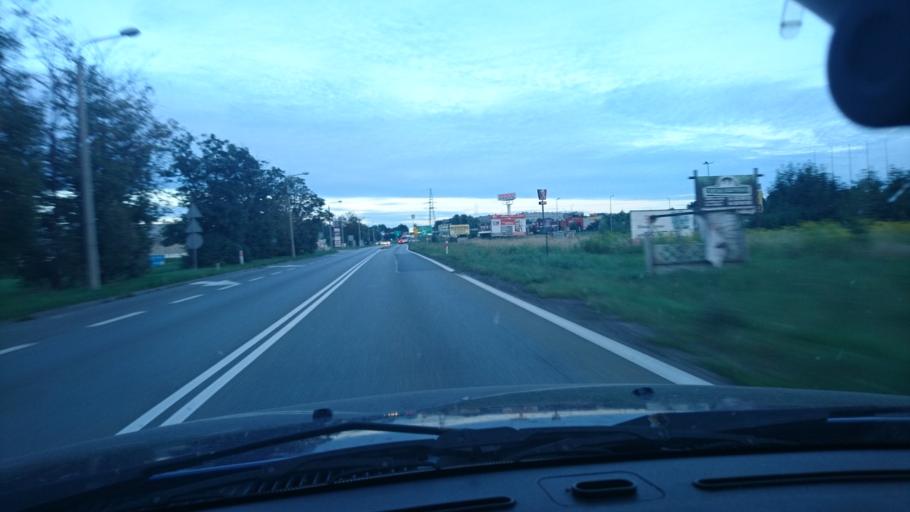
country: PL
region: Silesian Voivodeship
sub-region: Powiat tarnogorski
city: Tarnowskie Gory
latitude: 50.4561
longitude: 18.8334
